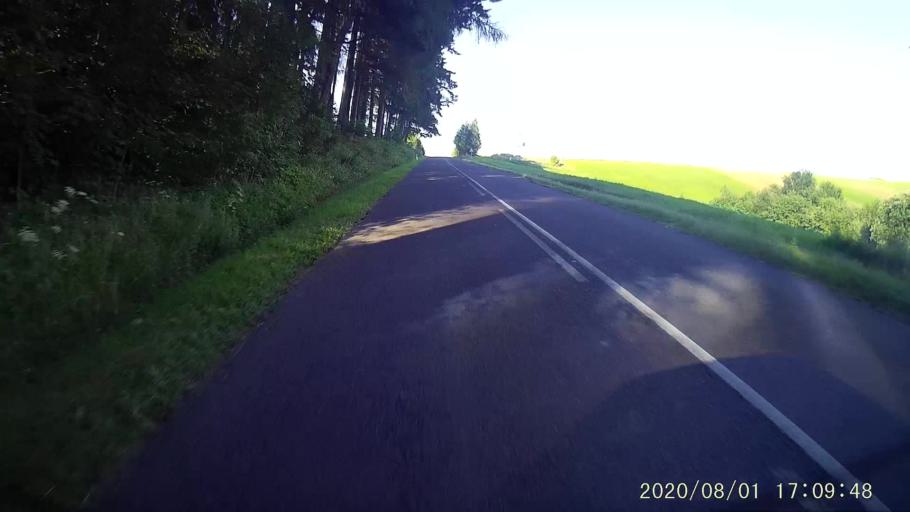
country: SK
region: Presovsky
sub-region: Okres Poprad
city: Zdiar
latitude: 49.2323
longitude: 20.3339
